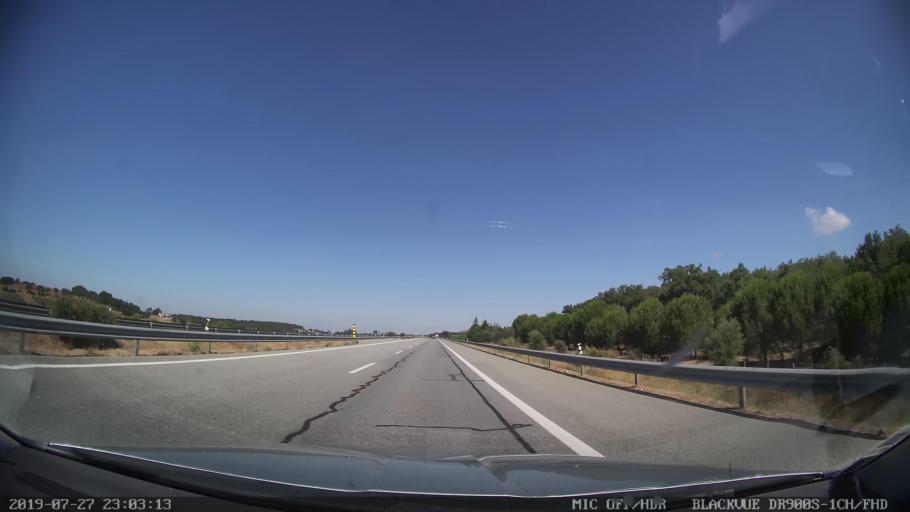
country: PT
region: Evora
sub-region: Estremoz
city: Estremoz
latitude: 38.8161
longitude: -7.5579
